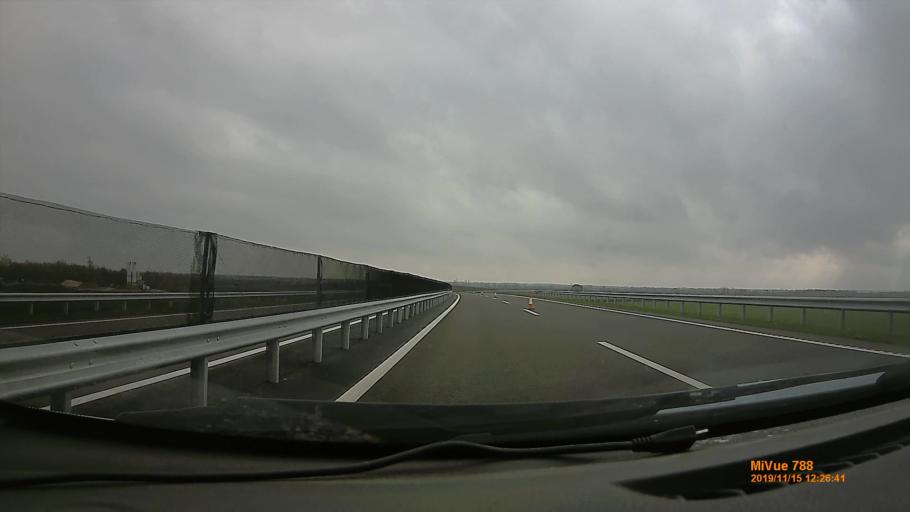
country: HU
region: Bekes
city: Kondoros
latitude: 46.7496
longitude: 20.7610
